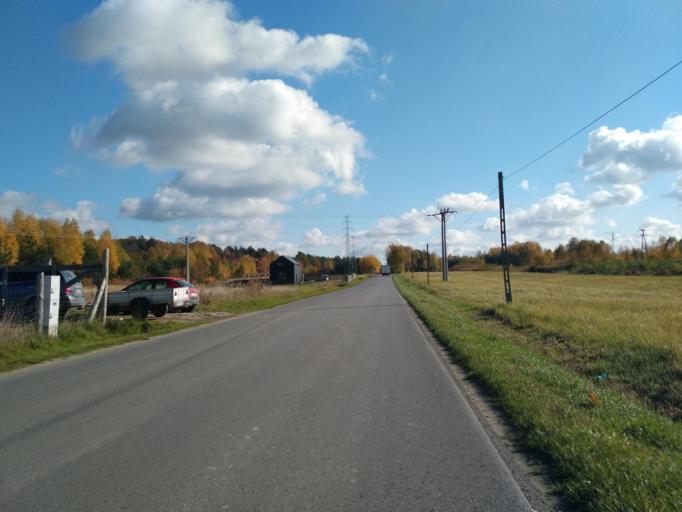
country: PL
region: Subcarpathian Voivodeship
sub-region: Powiat rzeszowski
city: Glogow Malopolski
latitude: 50.1574
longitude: 21.9186
